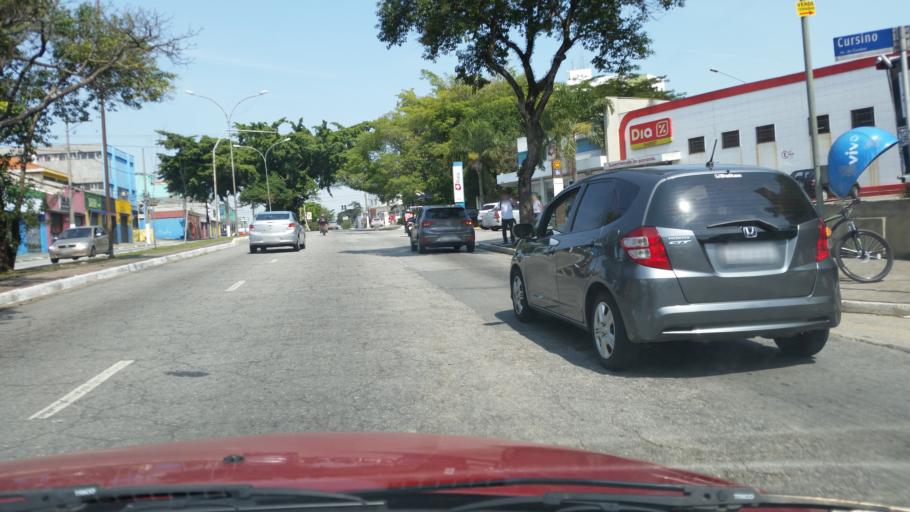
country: BR
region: Sao Paulo
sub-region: Diadema
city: Diadema
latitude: -23.6214
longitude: -46.6207
